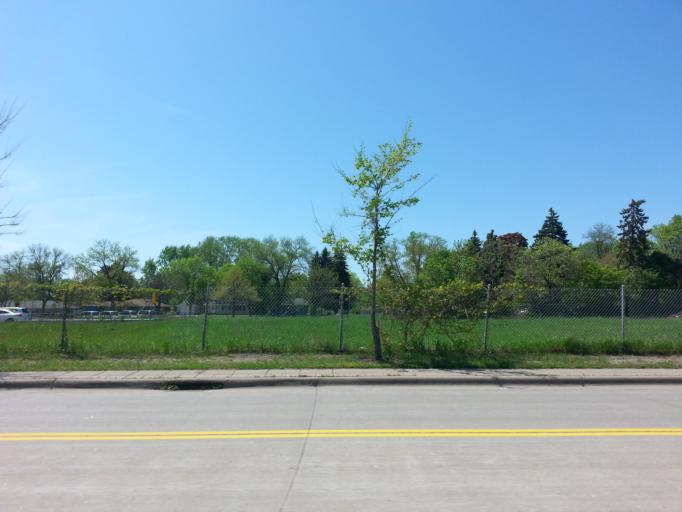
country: US
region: Minnesota
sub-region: Hennepin County
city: Richfield
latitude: 44.8778
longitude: -93.2464
